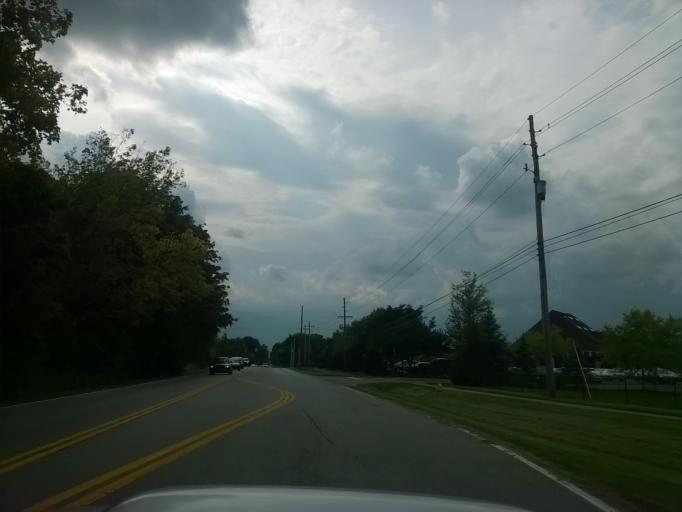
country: US
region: Indiana
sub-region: Hamilton County
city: Carmel
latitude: 39.9785
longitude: -86.0872
